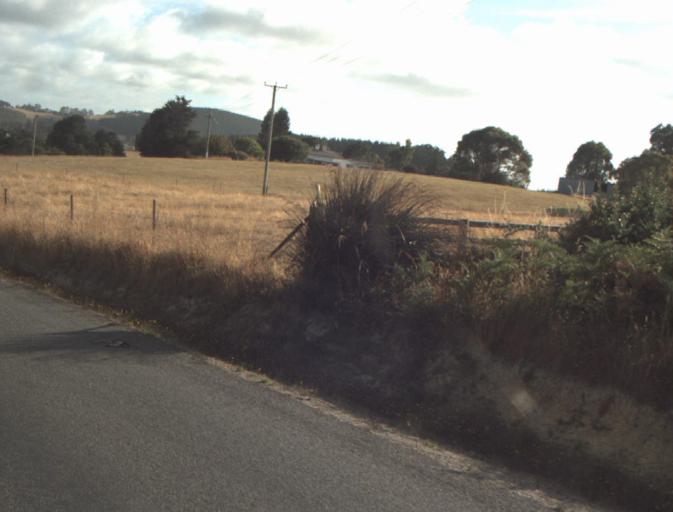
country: AU
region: Tasmania
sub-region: Launceston
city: Mayfield
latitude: -41.1939
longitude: 147.2209
